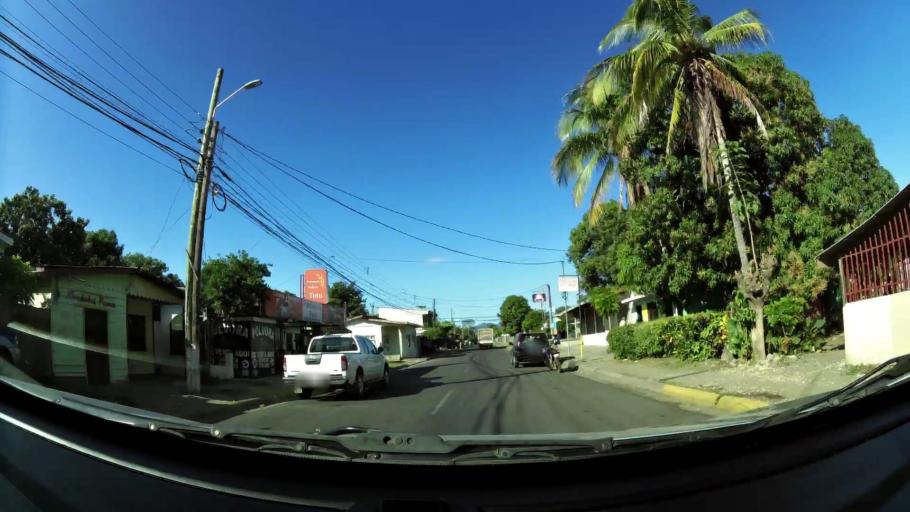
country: CR
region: Guanacaste
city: Belen
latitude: 10.4445
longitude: -85.5511
